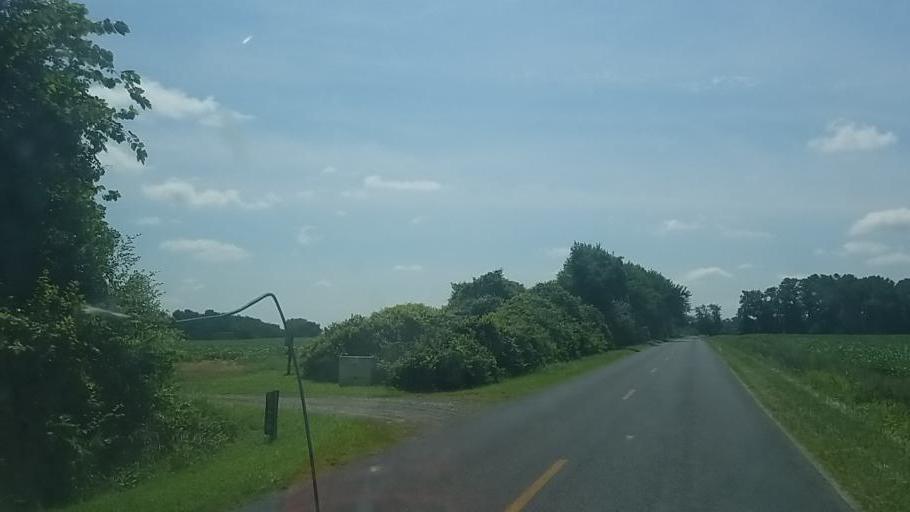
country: US
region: Maryland
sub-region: Caroline County
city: Ridgely
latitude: 38.9048
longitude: -75.9343
